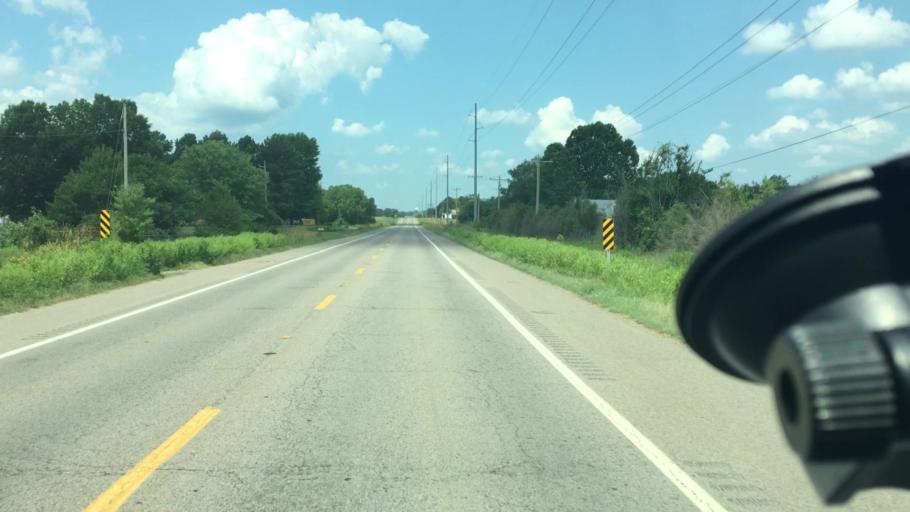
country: US
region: Arkansas
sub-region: Logan County
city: Paris
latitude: 35.2945
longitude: -93.6523
